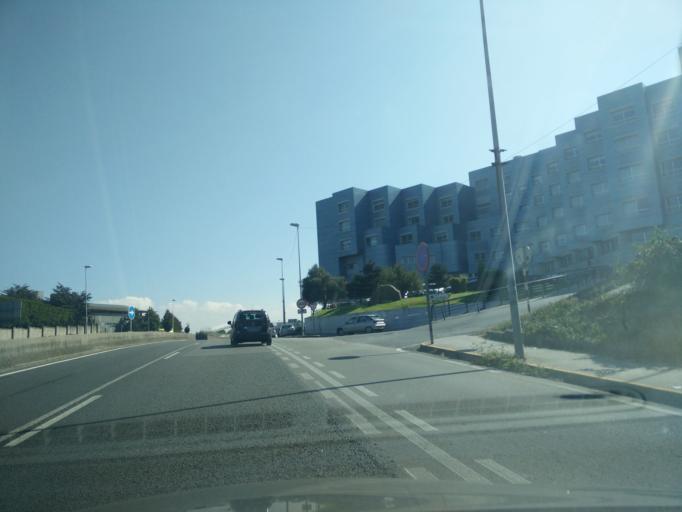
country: ES
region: Galicia
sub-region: Provincia da Coruna
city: A Coruna
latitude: 43.3460
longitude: -8.3880
